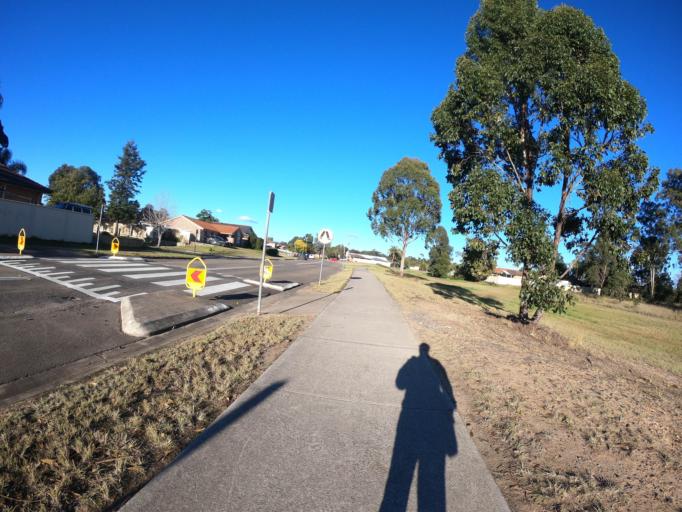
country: AU
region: New South Wales
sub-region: Hawkesbury
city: South Windsor
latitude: -33.6384
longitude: 150.8046
